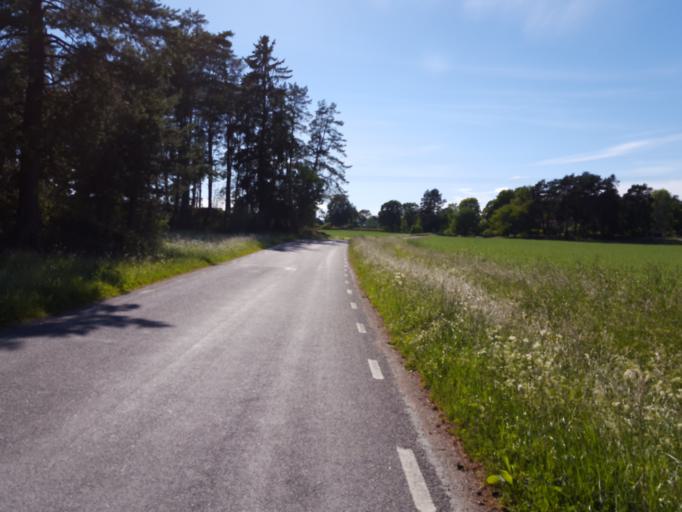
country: SE
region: Uppsala
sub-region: Uppsala Kommun
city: Saevja
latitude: 59.8291
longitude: 17.7587
